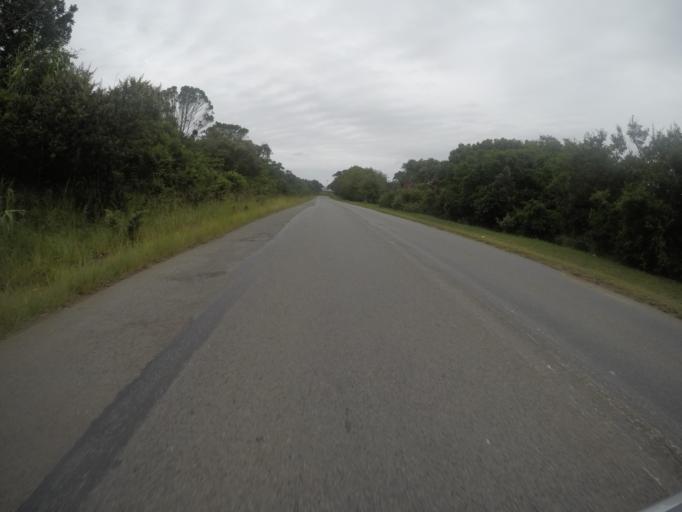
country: ZA
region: Eastern Cape
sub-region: Buffalo City Metropolitan Municipality
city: East London
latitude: -32.9463
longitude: 27.9284
